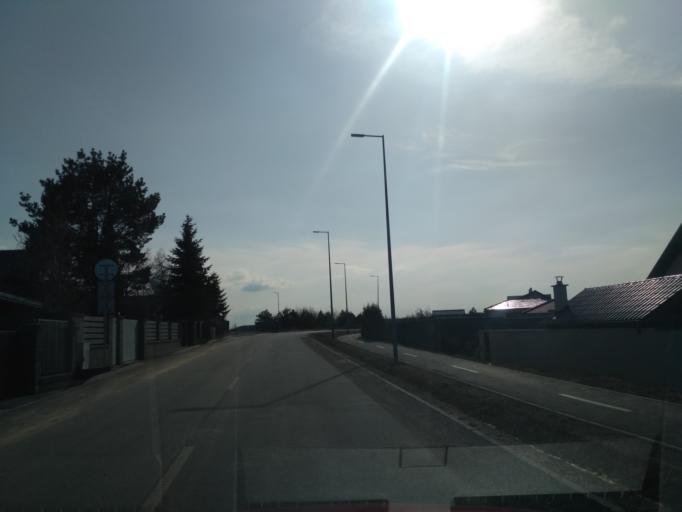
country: SK
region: Kosicky
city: Kosice
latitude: 48.6935
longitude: 21.2010
